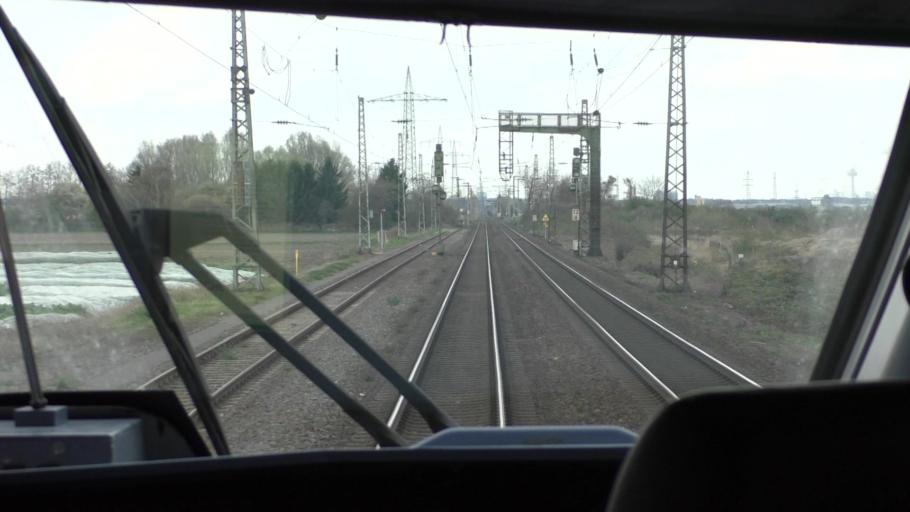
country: DE
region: North Rhine-Westphalia
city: Bruhl
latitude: 50.8469
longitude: 6.9089
